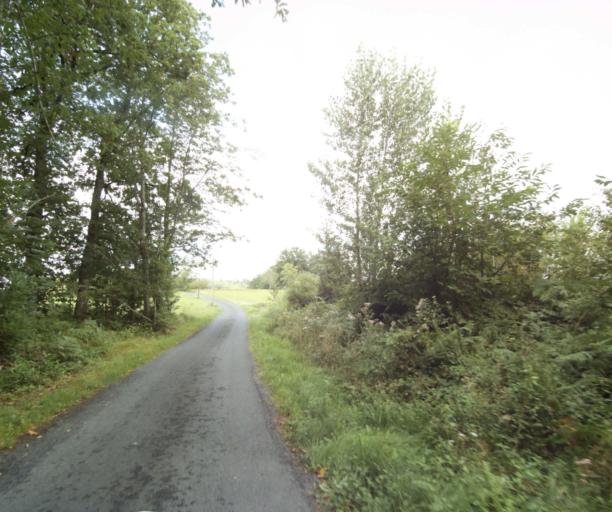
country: FR
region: Limousin
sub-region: Departement de la Correze
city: Sainte-Fortunade
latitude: 45.2117
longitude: 1.7906
